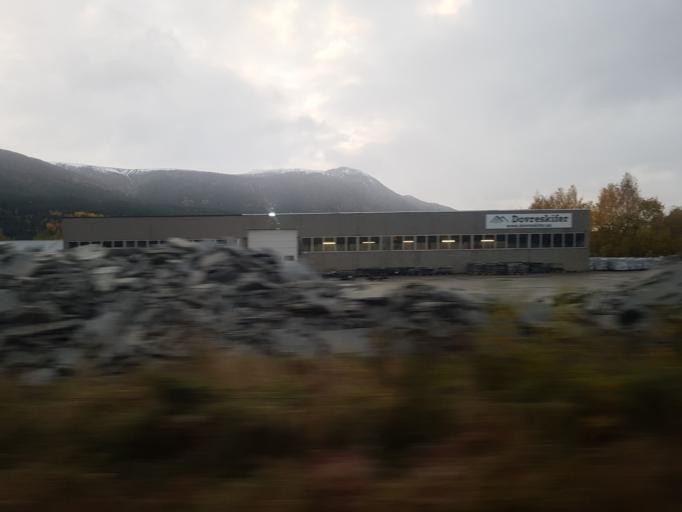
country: NO
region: Oppland
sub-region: Dovre
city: Dovre
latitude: 61.9926
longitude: 9.2370
